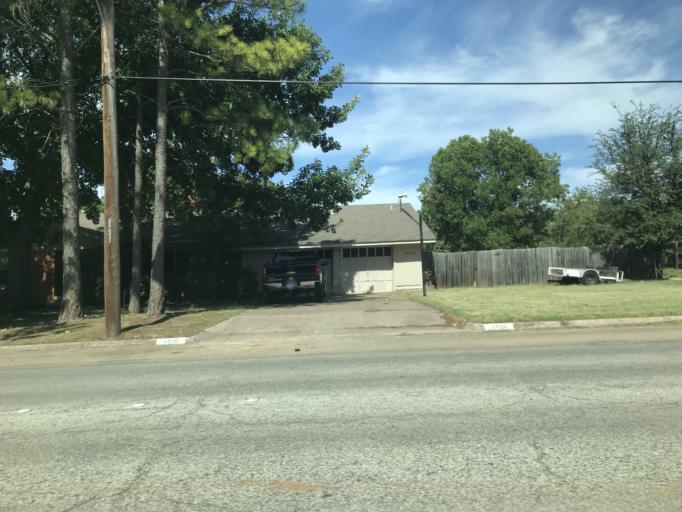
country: US
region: Texas
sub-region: Taylor County
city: Abilene
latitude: 32.4233
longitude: -99.7494
